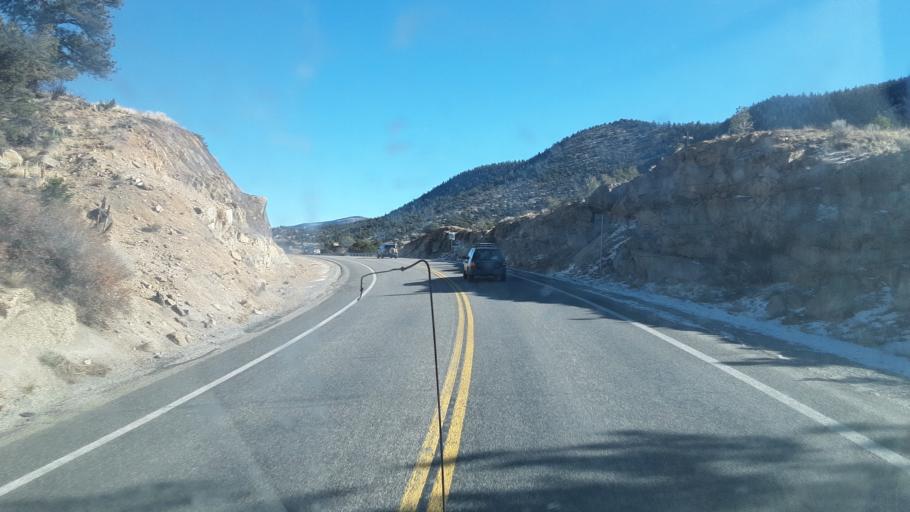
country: US
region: Colorado
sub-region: Chaffee County
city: Buena Vista
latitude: 38.8276
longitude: -106.0375
